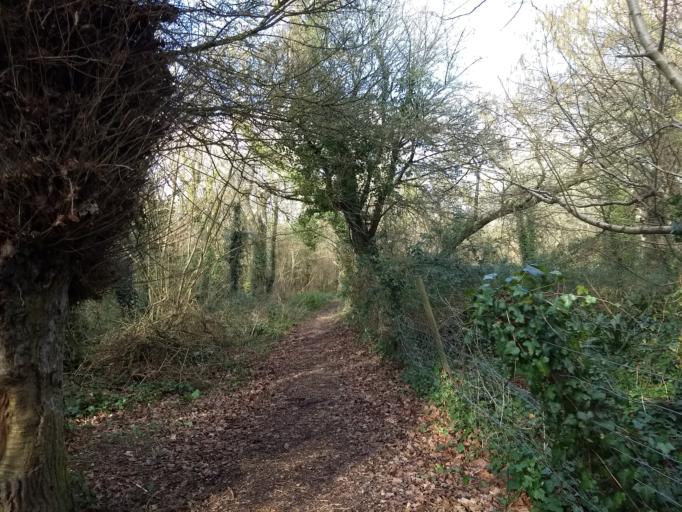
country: GB
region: England
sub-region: Isle of Wight
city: Bembridge
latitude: 50.6787
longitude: -1.0960
